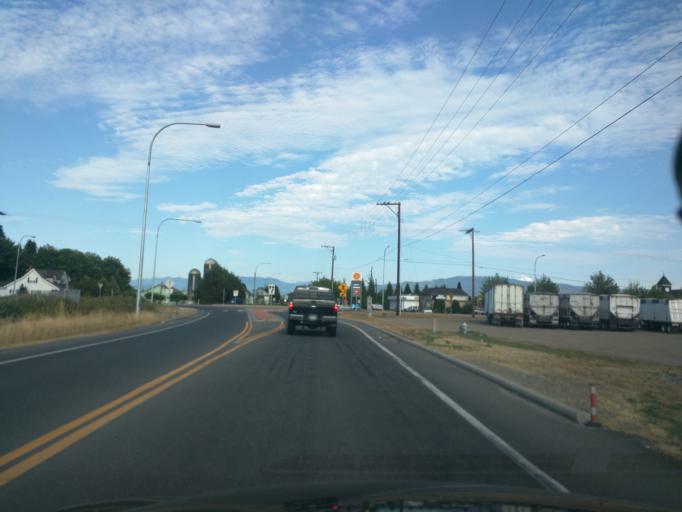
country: US
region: Washington
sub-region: Whatcom County
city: Lynden
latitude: 48.9644
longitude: -122.4425
